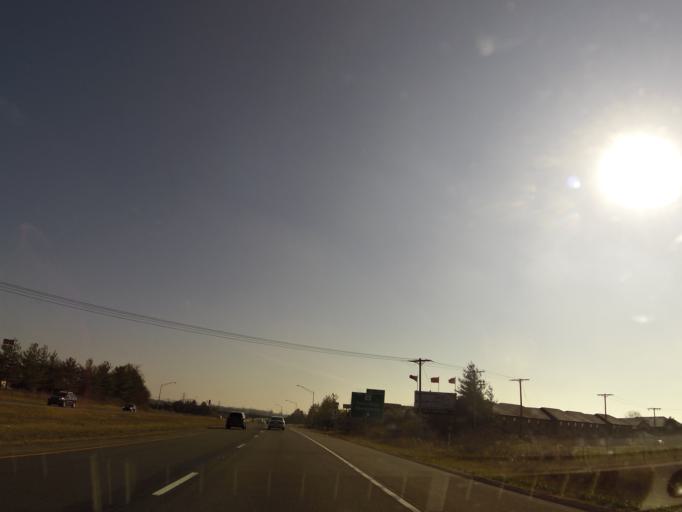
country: US
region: Indiana
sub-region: Shelby County
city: Shelbyville
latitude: 39.5532
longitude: -85.7810
